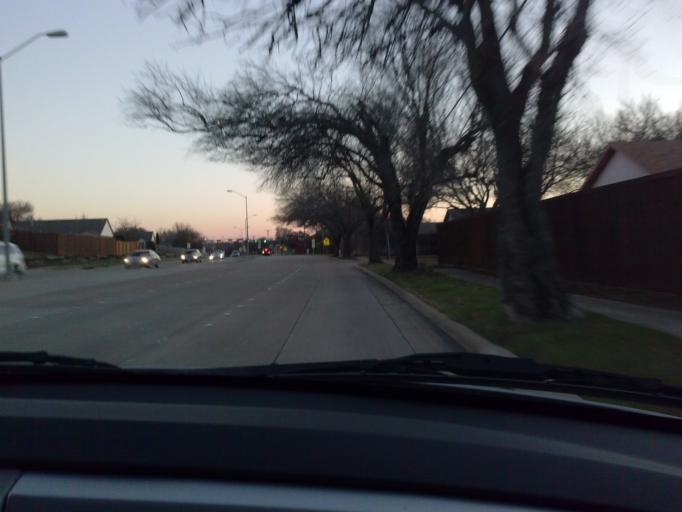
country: US
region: Texas
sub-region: Collin County
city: Allen
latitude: 33.0807
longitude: -96.7124
